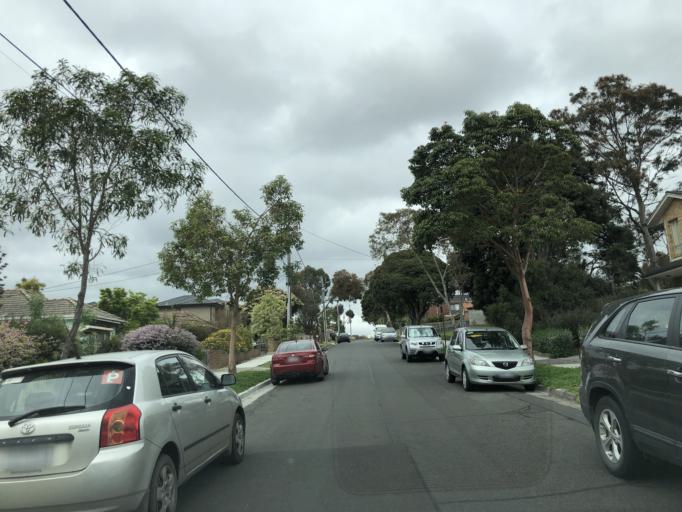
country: AU
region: Victoria
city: Burwood East
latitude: -37.8445
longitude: 145.1375
